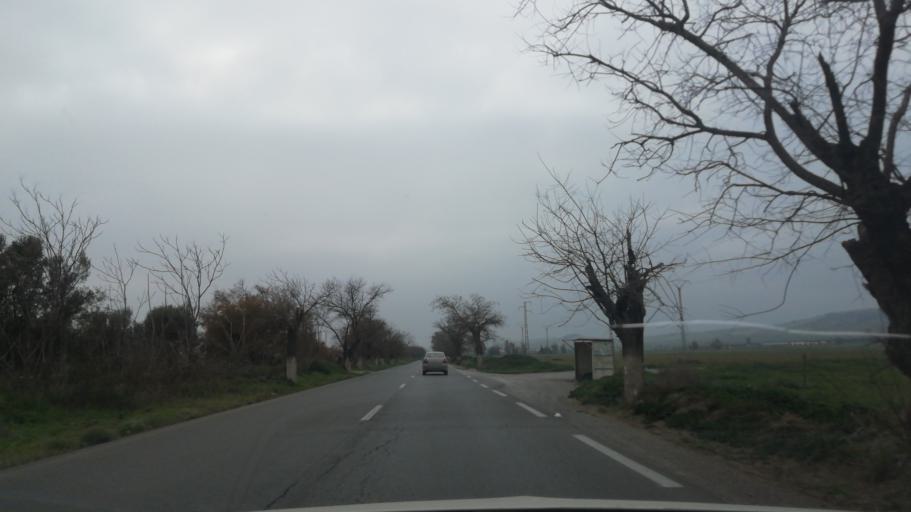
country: DZ
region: Sidi Bel Abbes
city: Sfizef
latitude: 35.2226
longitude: -0.2860
